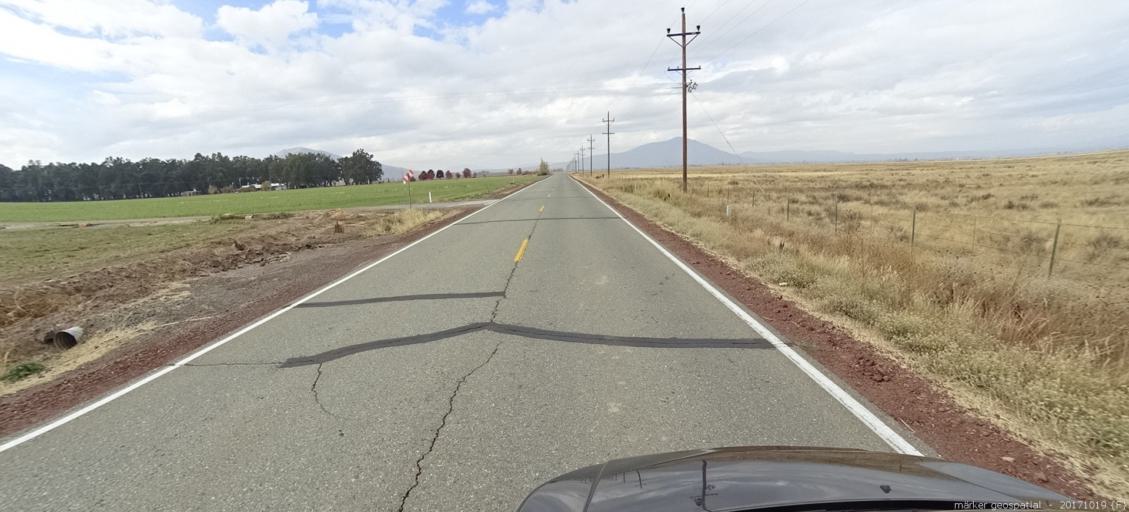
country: US
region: California
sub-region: Shasta County
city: Burney
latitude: 41.0509
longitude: -121.4121
